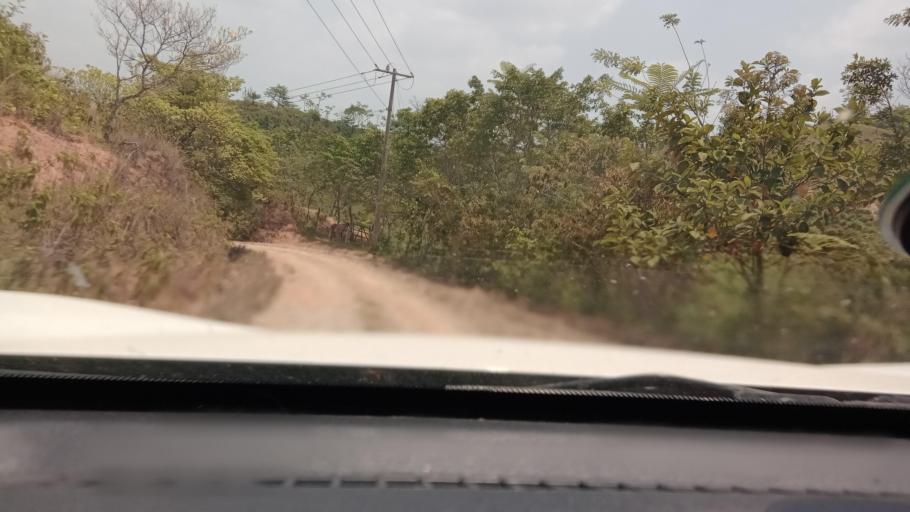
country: MX
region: Tabasco
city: Chontalpa
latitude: 17.5572
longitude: -93.7295
